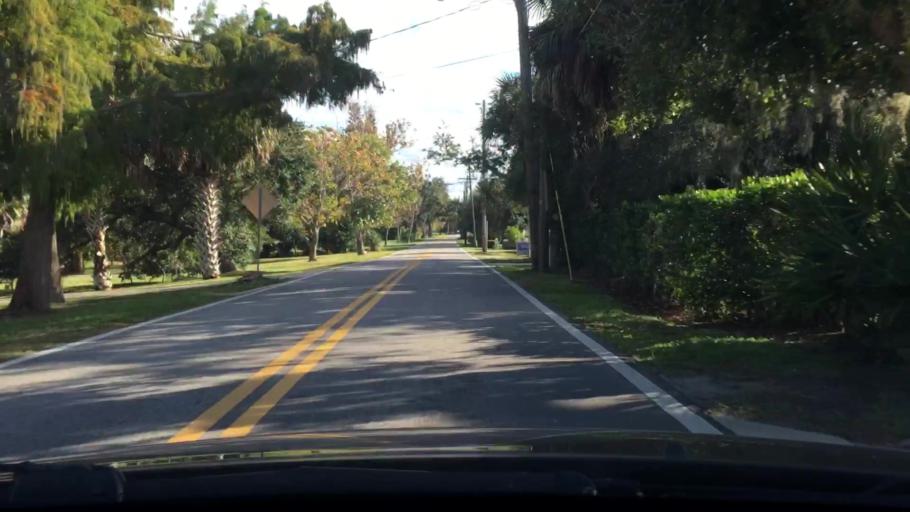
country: US
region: Florida
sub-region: Volusia County
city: Ormond Beach
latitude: 29.3086
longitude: -81.0567
